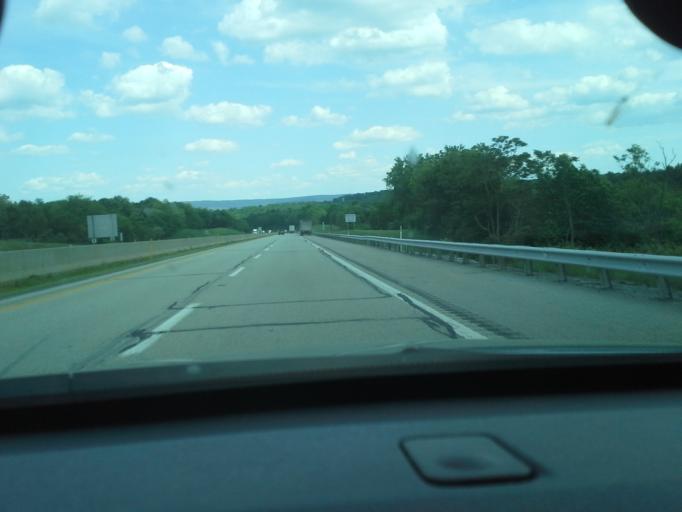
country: US
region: Pennsylvania
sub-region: Fulton County
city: McConnellsburg
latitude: 40.0482
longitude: -78.0654
